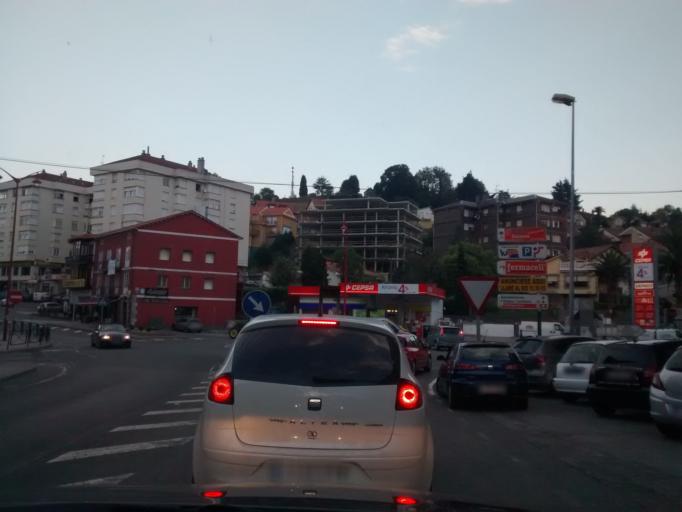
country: ES
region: Cantabria
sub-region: Provincia de Cantabria
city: Lierganes
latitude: 43.3838
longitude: -3.7384
